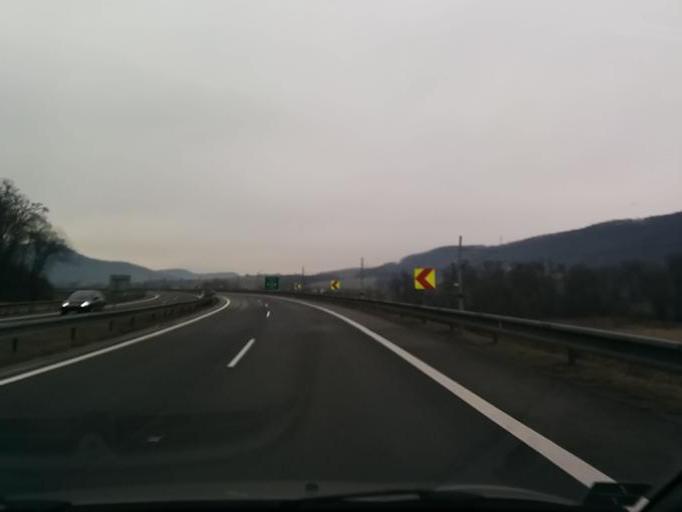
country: SK
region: Banskobystricky
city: Zarnovica
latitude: 48.4414
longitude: 18.6964
